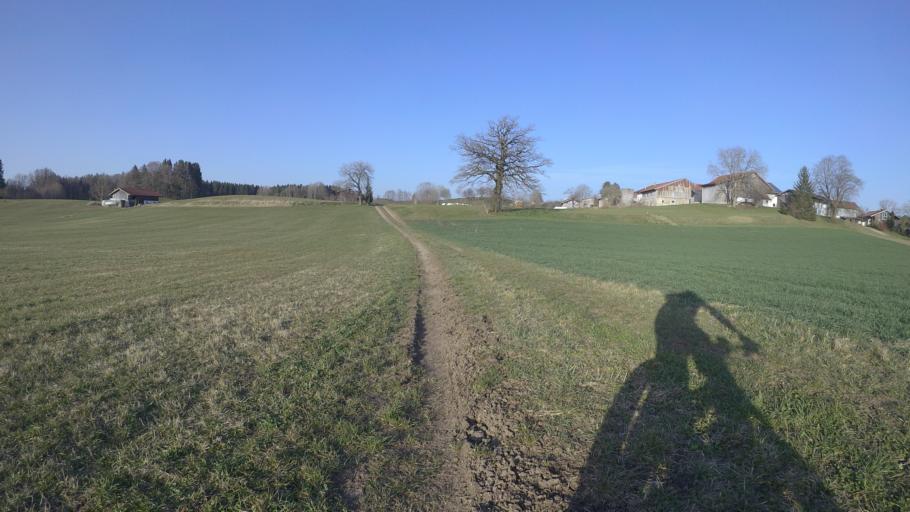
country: DE
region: Bavaria
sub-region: Upper Bavaria
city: Nussdorf
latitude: 47.9197
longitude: 12.5640
